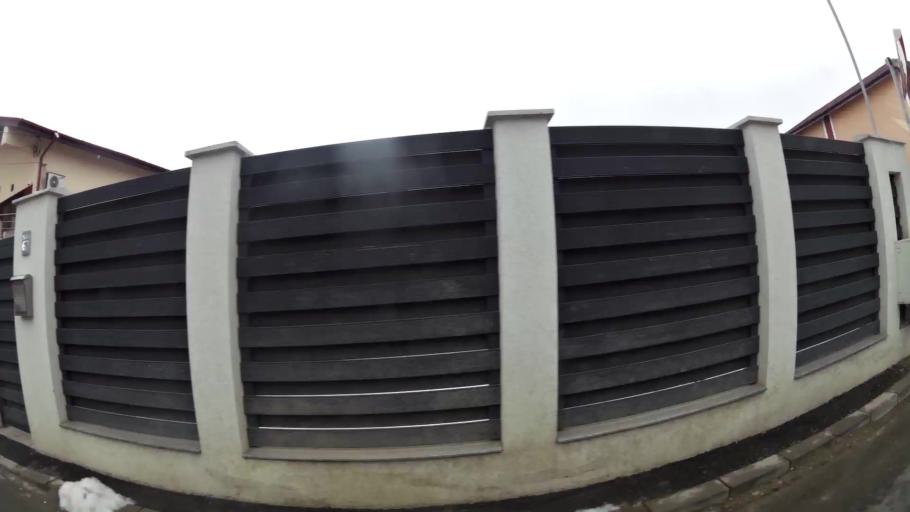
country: RO
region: Ilfov
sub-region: Comuna Otopeni
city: Otopeni
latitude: 44.5538
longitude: 26.0949
